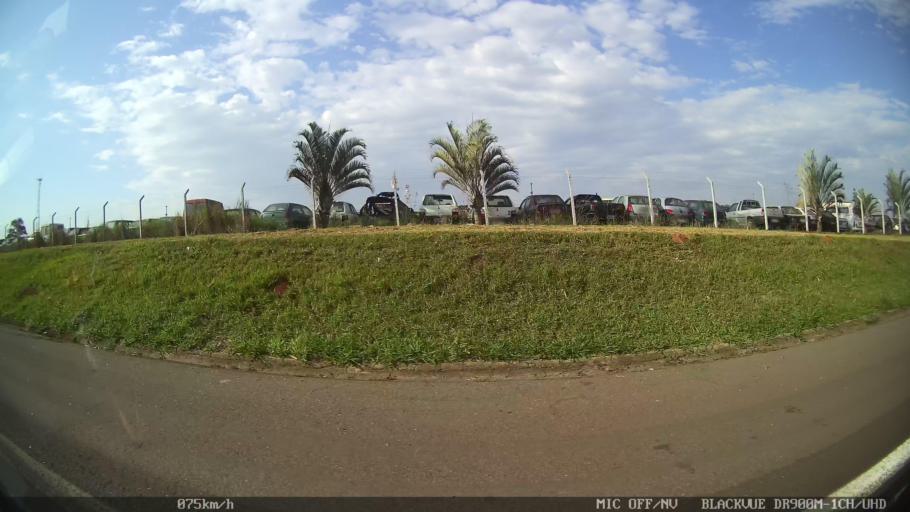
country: BR
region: Sao Paulo
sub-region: Cosmopolis
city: Cosmopolis
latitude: -22.6750
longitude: -47.1602
